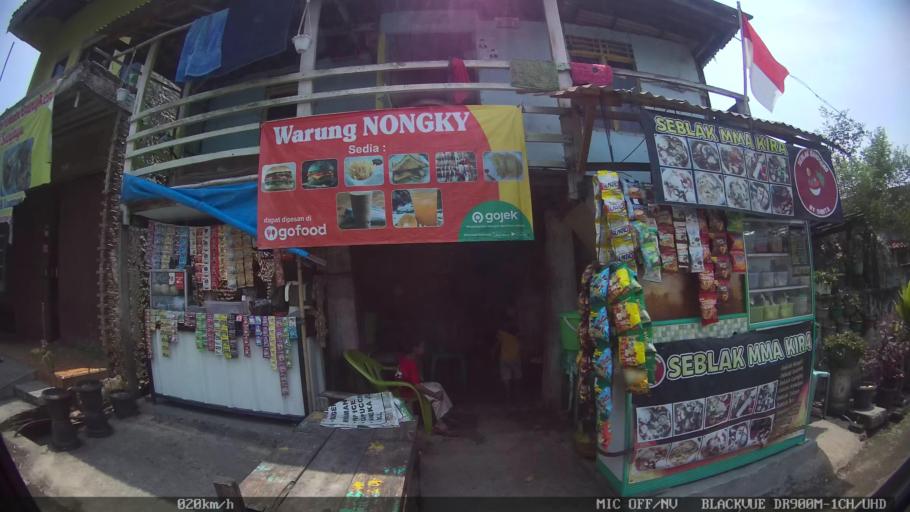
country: ID
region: Lampung
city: Bandarlampung
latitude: -5.4563
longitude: 105.2623
